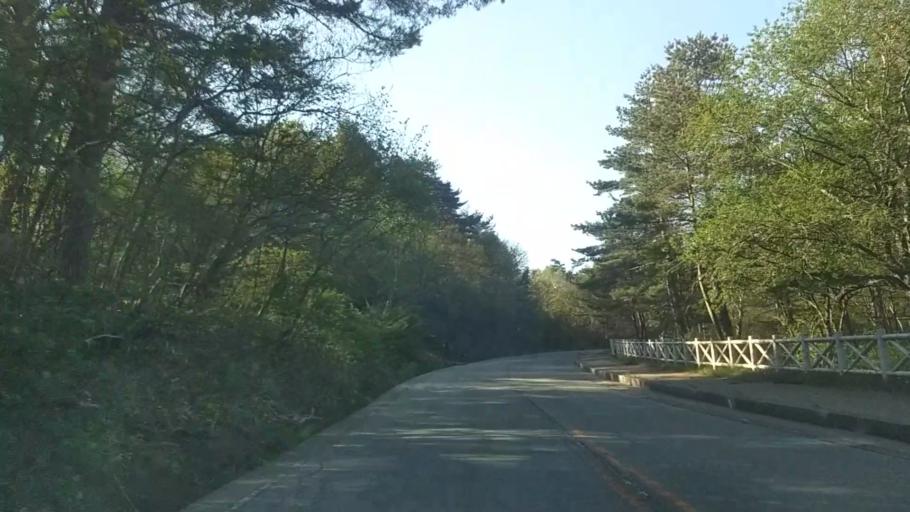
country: JP
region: Yamanashi
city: Nirasaki
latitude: 35.9260
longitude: 138.4073
